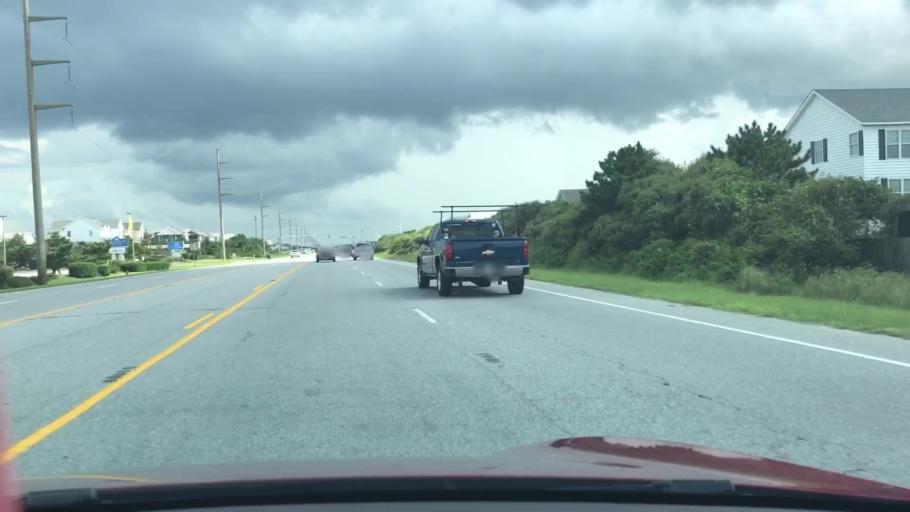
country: US
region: North Carolina
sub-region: Dare County
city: Nags Head
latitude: 35.9433
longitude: -75.6190
